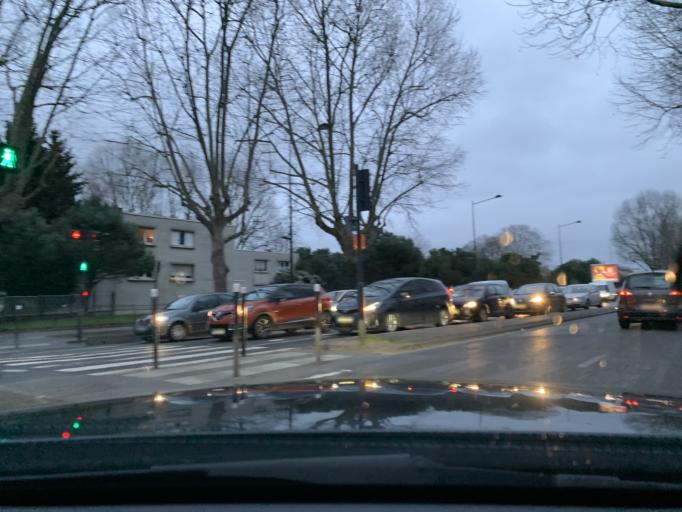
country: FR
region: Ile-de-France
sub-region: Departement de Seine-Saint-Denis
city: Saint-Denis
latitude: 48.9420
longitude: 2.3654
